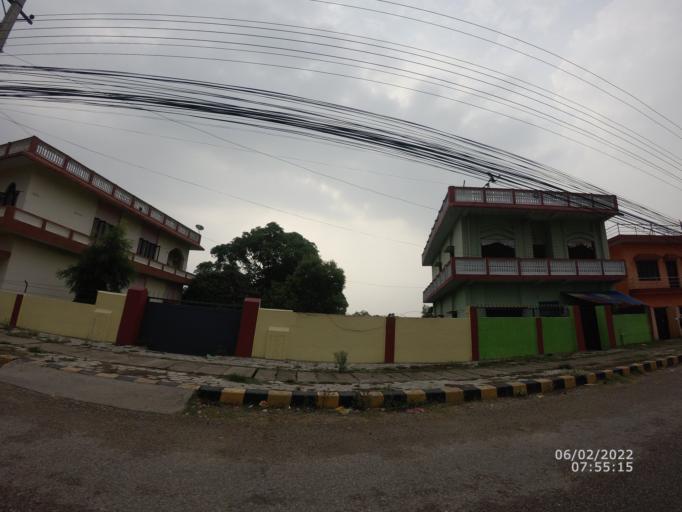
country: NP
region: Western Region
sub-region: Lumbini Zone
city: Bhairahawa
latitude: 27.4962
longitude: 83.4594
